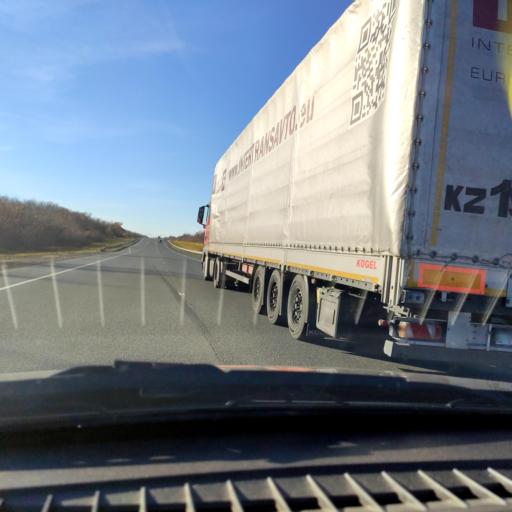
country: RU
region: Samara
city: Mezhdurechensk
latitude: 53.2574
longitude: 49.1136
